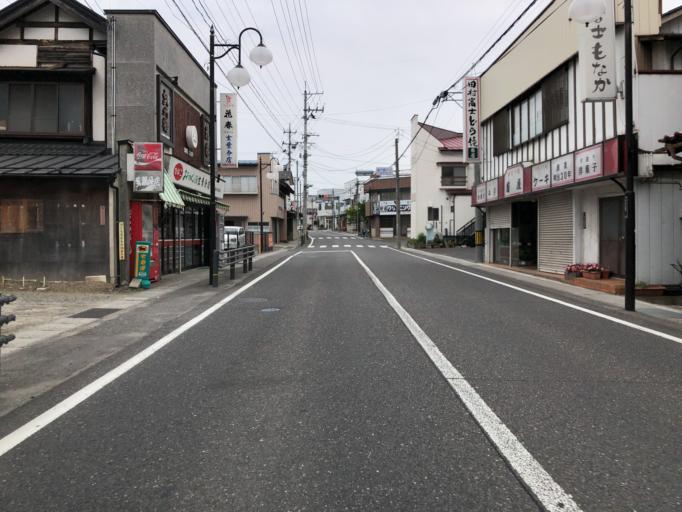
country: JP
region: Fukushima
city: Funehikimachi-funehiki
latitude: 37.4389
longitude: 140.5734
